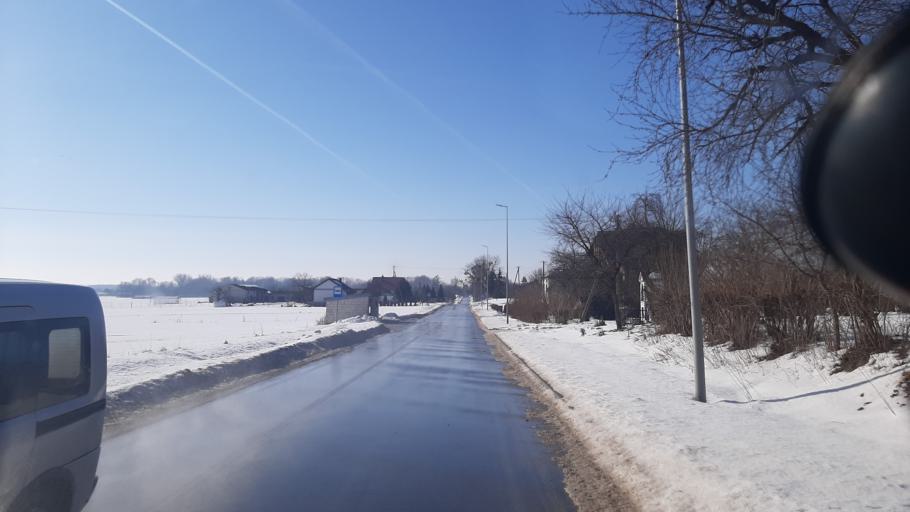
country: PL
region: Lublin Voivodeship
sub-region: Powiat lubelski
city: Garbow
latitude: 51.3268
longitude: 22.3275
